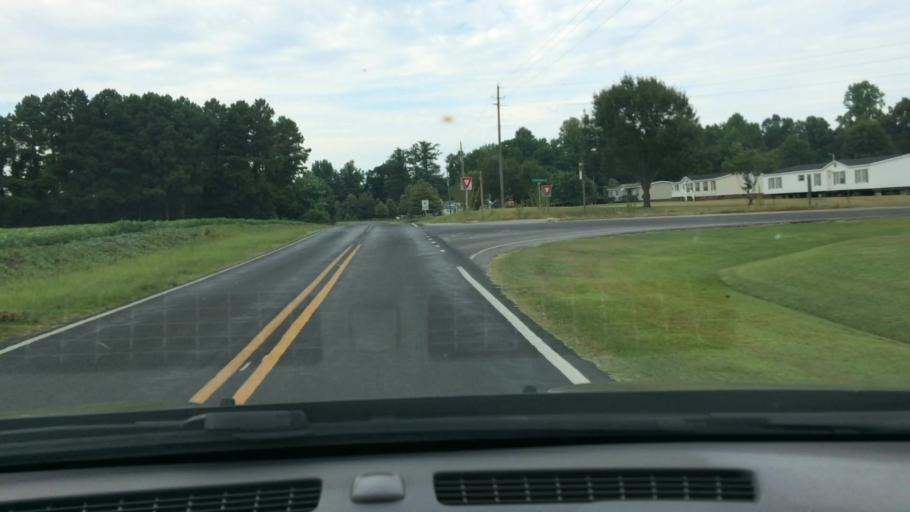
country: US
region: North Carolina
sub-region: Pitt County
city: Ayden
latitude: 35.4474
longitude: -77.4109
